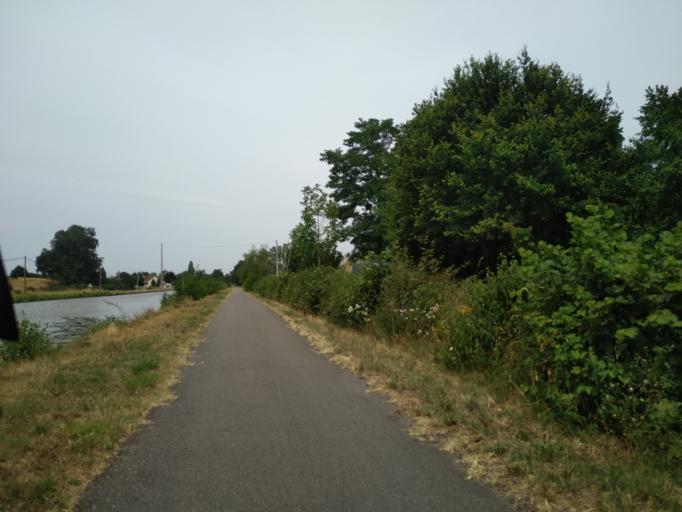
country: FR
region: Auvergne
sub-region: Departement de l'Allier
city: Molinet
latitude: 46.4723
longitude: 3.9399
